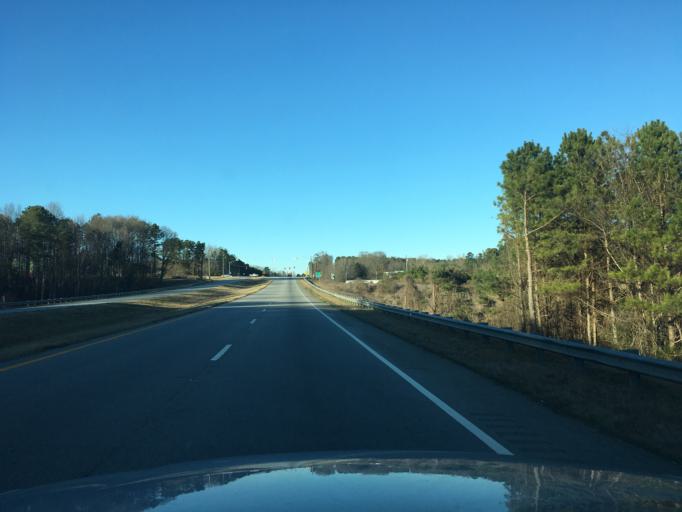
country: US
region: Georgia
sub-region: Carroll County
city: Carrollton
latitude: 33.4565
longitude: -85.1241
